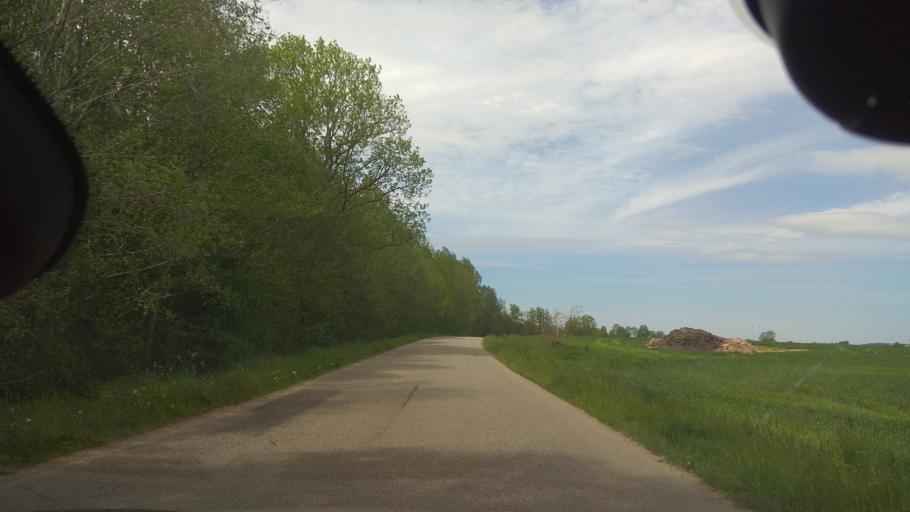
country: LT
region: Vilnius County
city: Ukmerge
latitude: 55.1517
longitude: 24.5489
